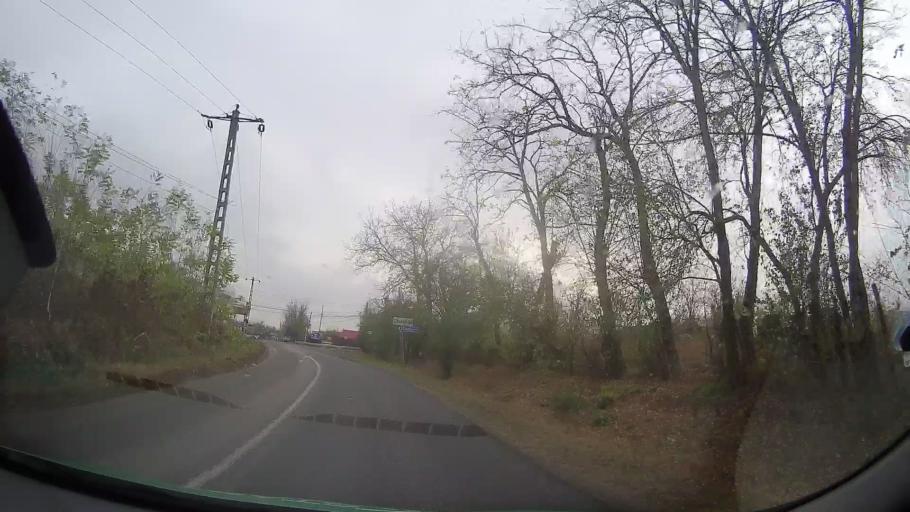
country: RO
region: Prahova
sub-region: Comuna Gherghita
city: Gherghita
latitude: 44.8012
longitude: 26.2669
